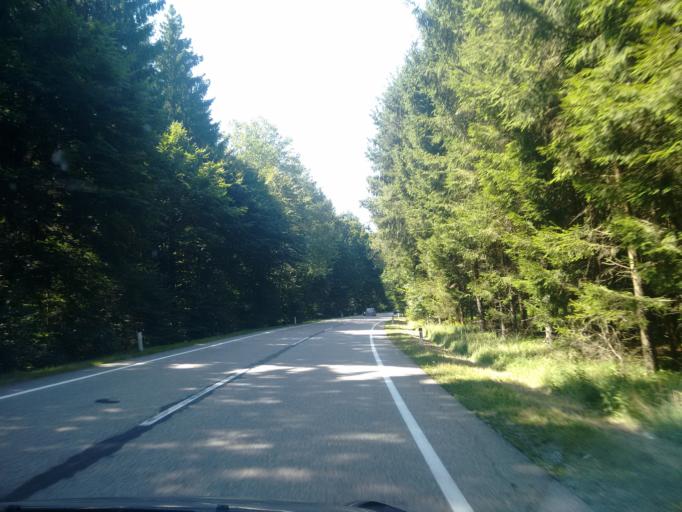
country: DE
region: Bavaria
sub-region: Lower Bavaria
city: Julbach
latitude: 48.2024
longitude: 12.9491
